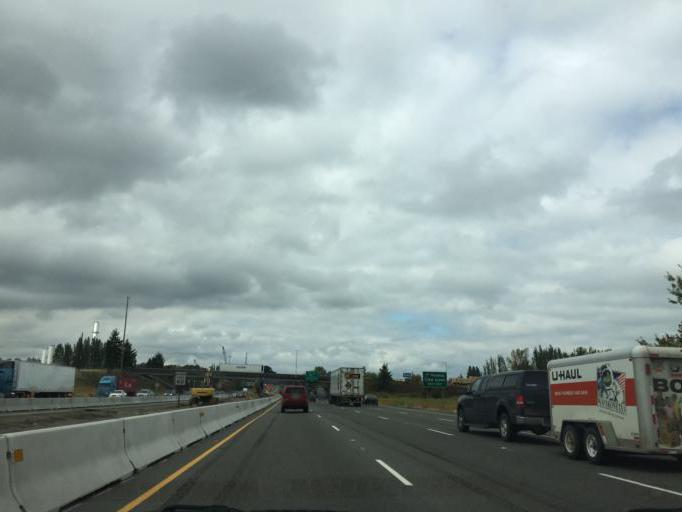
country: US
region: Washington
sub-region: Pierce County
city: Fife
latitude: 47.2411
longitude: -122.3826
